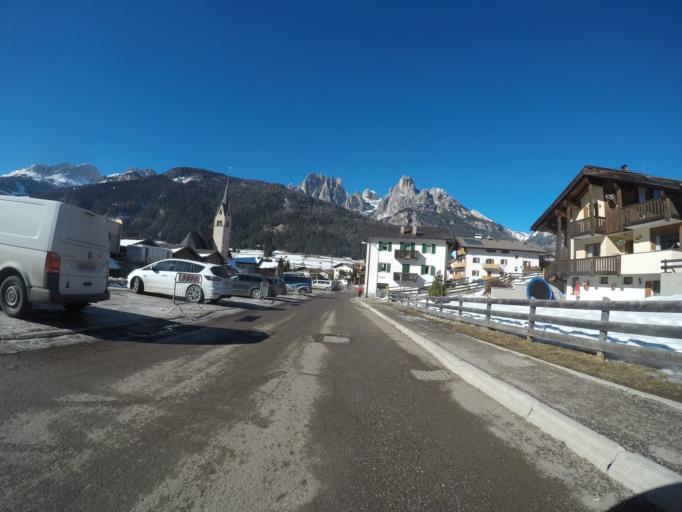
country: IT
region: Trentino-Alto Adige
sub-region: Provincia di Trento
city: Pozza di Fassa
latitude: 46.4292
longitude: 11.6959
